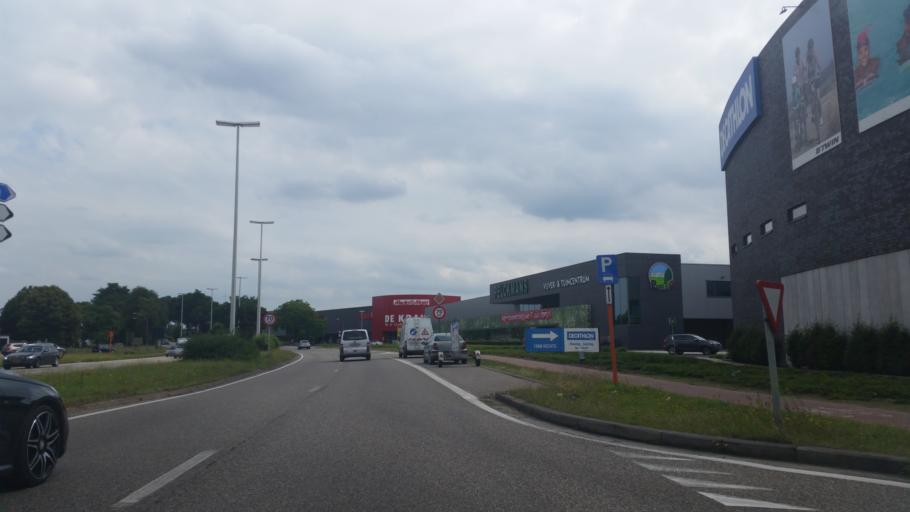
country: BE
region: Flanders
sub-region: Provincie Antwerpen
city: Turnhout
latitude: 51.3135
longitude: 4.9257
